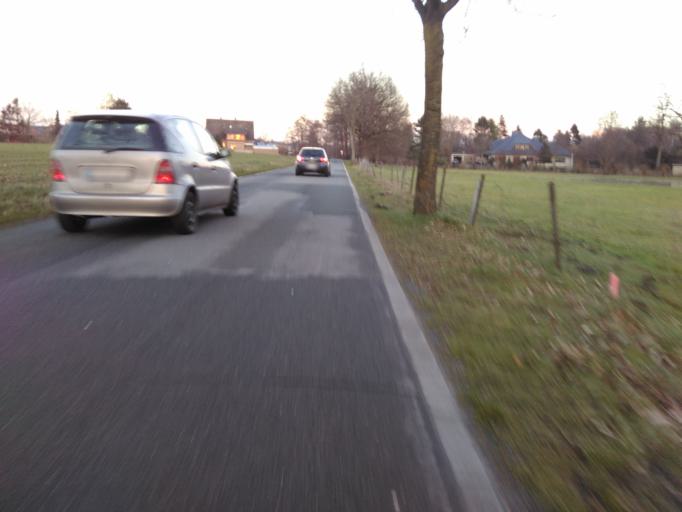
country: DE
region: North Rhine-Westphalia
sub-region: Regierungsbezirk Detmold
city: Verl
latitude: 51.8694
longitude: 8.4914
